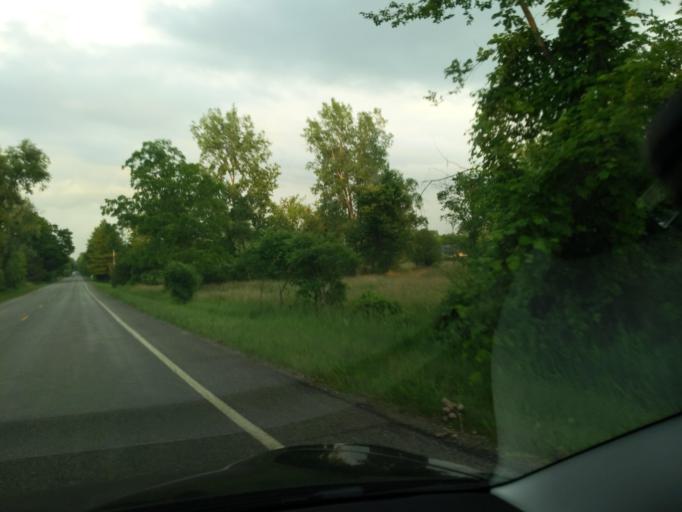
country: US
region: Michigan
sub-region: Ingham County
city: Mason
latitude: 42.5239
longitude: -84.4112
